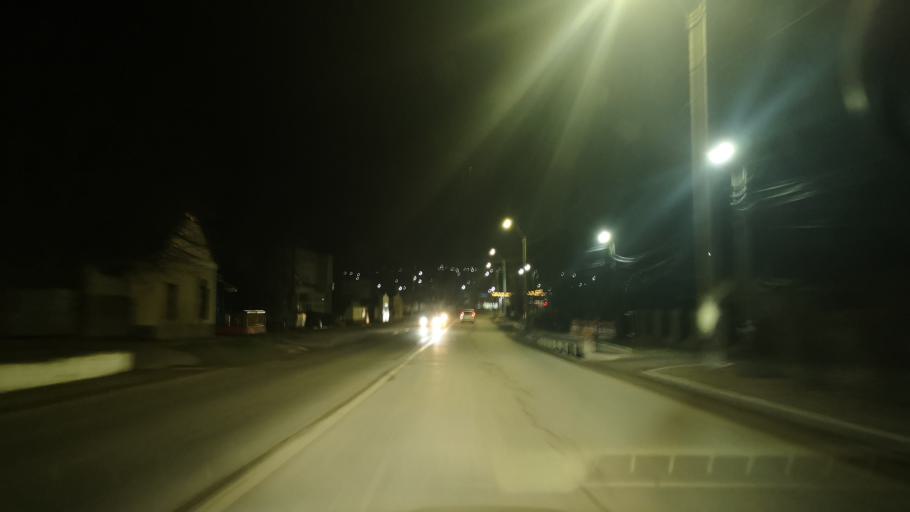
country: MD
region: Orhei
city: Orhei
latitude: 47.3581
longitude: 28.8125
